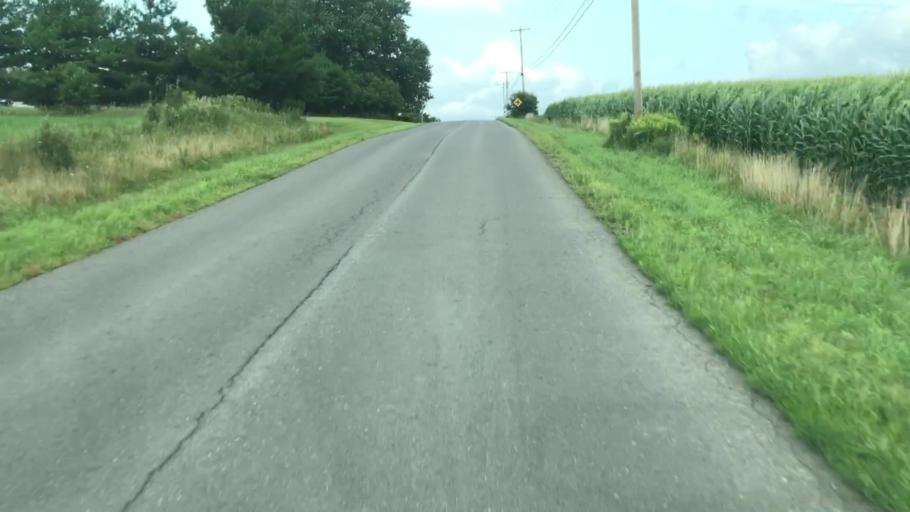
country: US
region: New York
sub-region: Onondaga County
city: Elbridge
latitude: 42.9853
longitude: -76.4978
